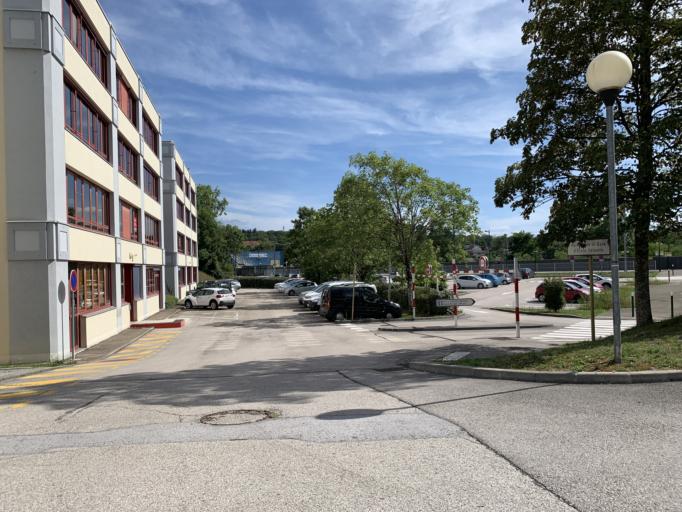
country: FR
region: Franche-Comte
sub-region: Departement du Doubs
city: Miserey-Salines
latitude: 47.2760
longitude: 5.9937
